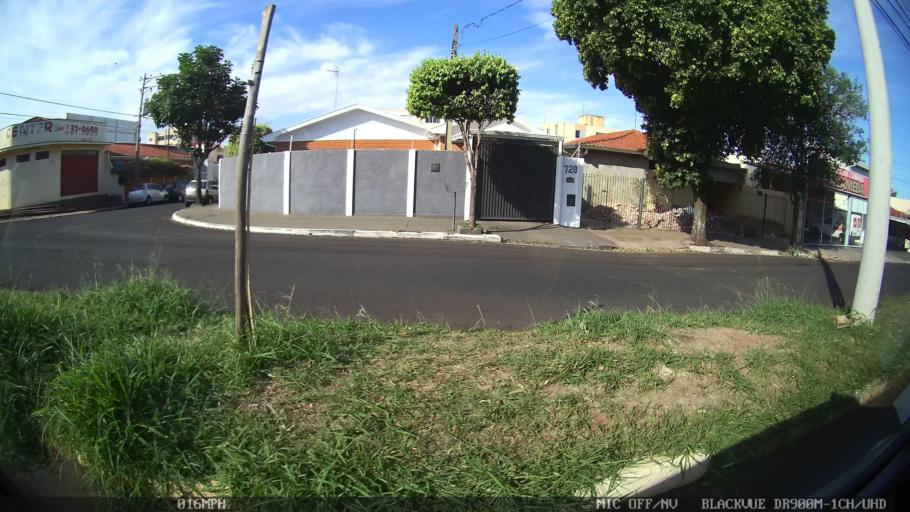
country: BR
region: Sao Paulo
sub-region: Araraquara
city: Araraquara
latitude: -21.7858
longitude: -48.1579
